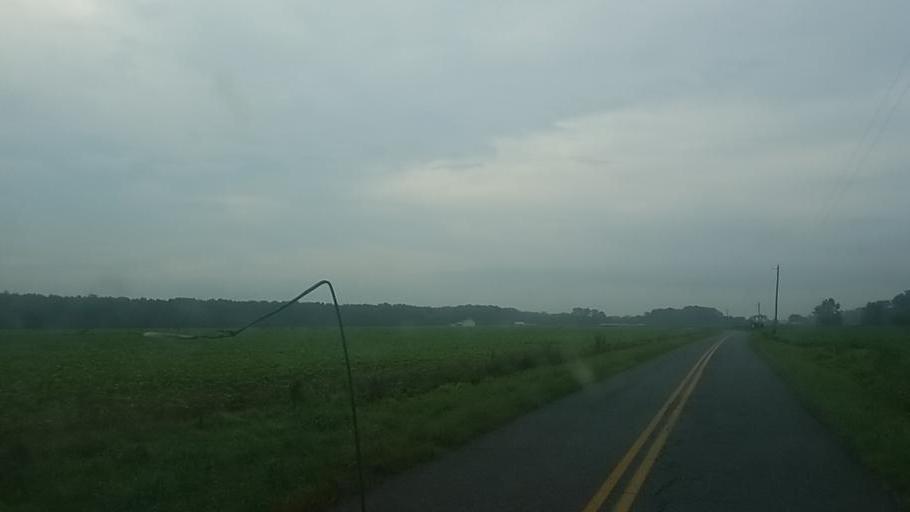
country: US
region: Maryland
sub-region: Wicomico County
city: Pittsville
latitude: 38.4262
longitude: -75.3215
